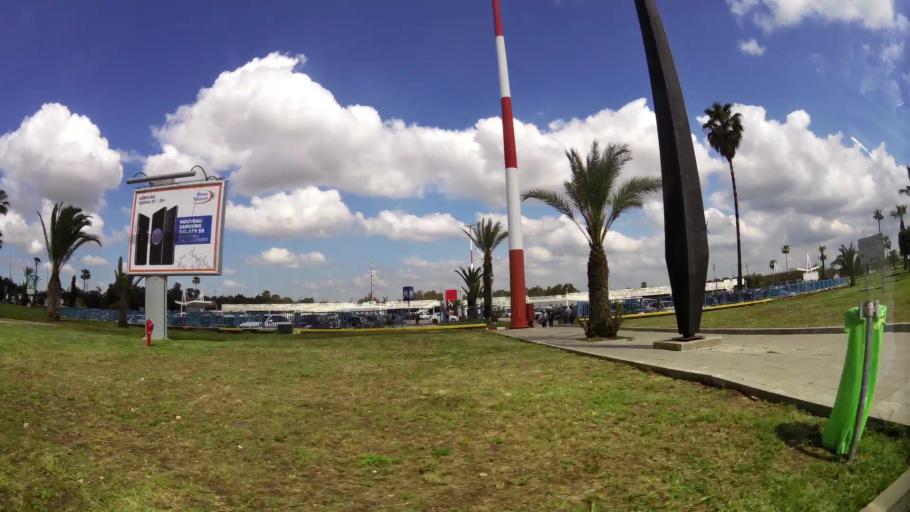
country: MA
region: Chaouia-Ouardigha
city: Nouaseur
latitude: 33.3753
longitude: -7.5809
